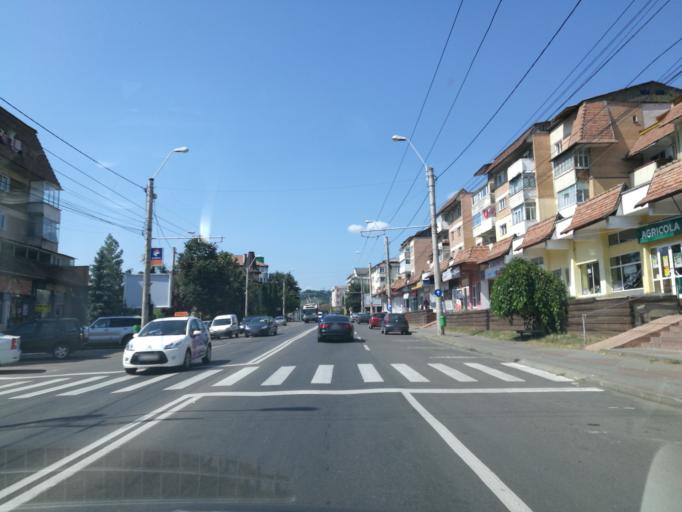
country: RO
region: Neamt
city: Piatra Neamt
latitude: 46.9359
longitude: 26.3517
